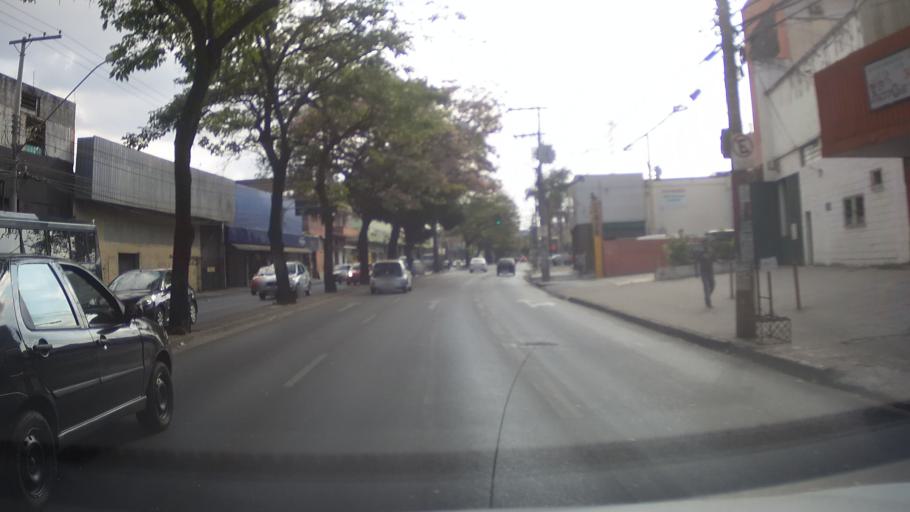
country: BR
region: Minas Gerais
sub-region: Belo Horizonte
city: Belo Horizonte
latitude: -19.9107
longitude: -43.9672
